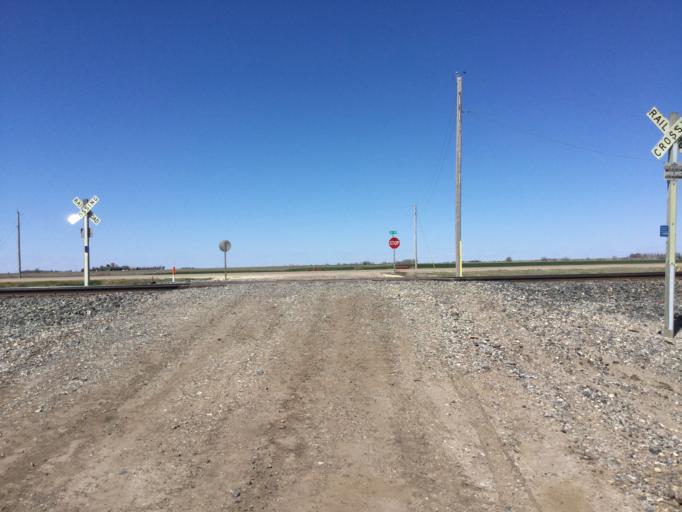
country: US
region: Kansas
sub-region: Edwards County
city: Kinsley
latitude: 37.9050
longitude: -99.4780
